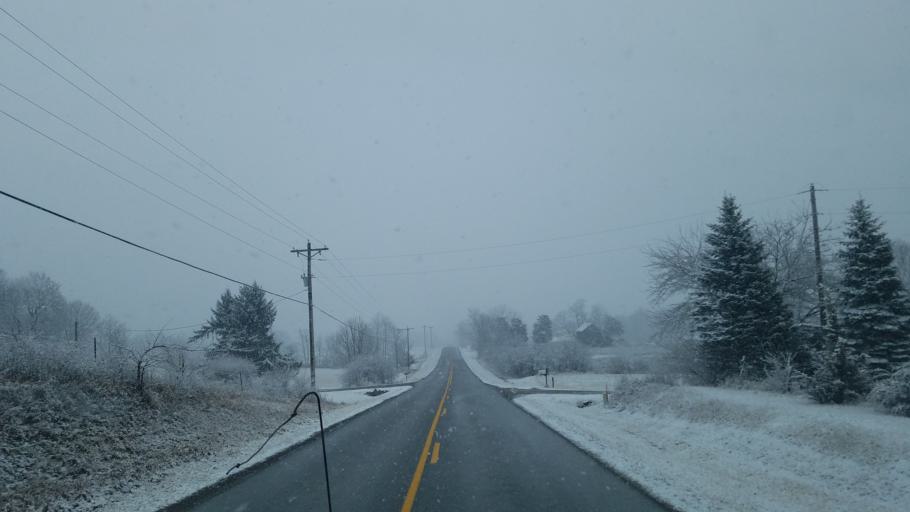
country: US
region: Ohio
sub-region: Champaign County
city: North Lewisburg
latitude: 40.3394
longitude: -83.6144
